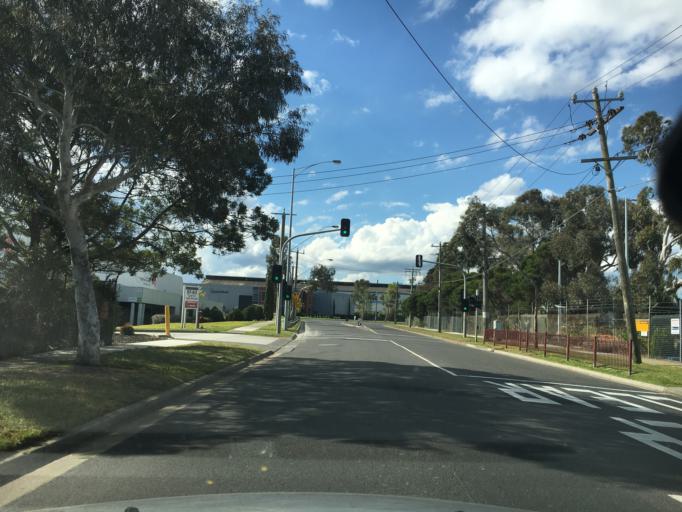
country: AU
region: Victoria
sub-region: Monash
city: Clayton
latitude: -37.9294
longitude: 145.1362
